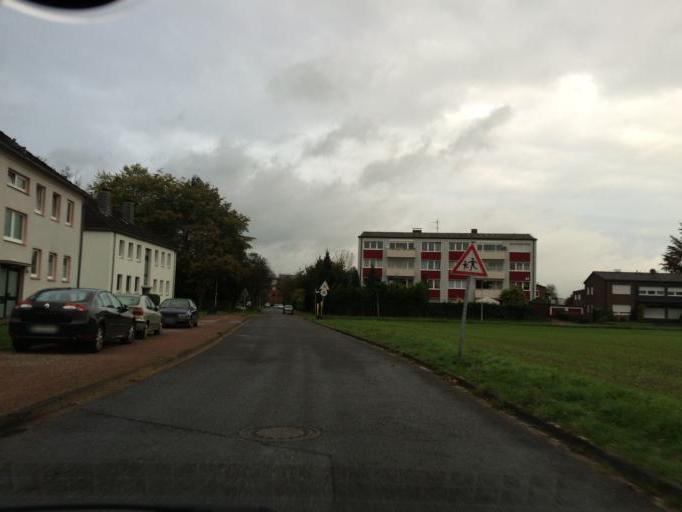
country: DE
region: North Rhine-Westphalia
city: Dorsten
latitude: 51.6718
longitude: 6.9988
